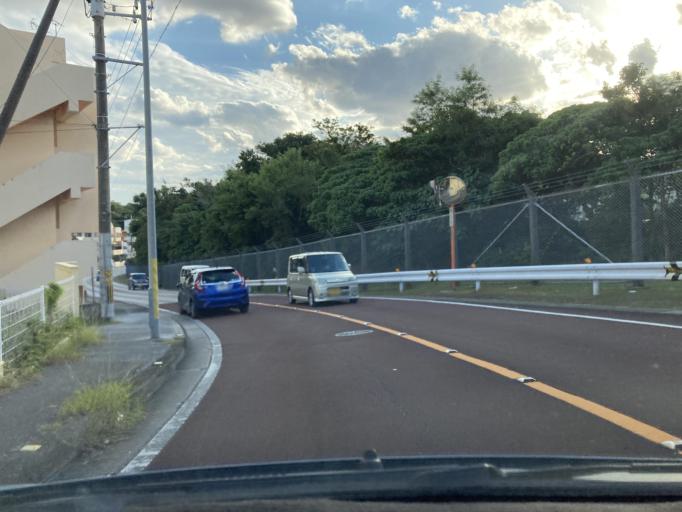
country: JP
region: Okinawa
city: Chatan
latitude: 26.3152
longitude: 127.7674
